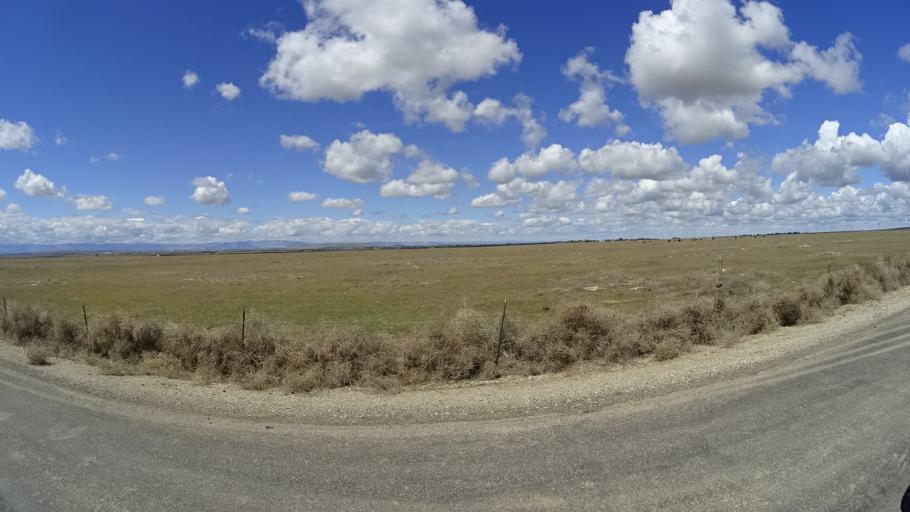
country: US
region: Idaho
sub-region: Ada County
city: Kuna
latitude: 43.4708
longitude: -116.2744
